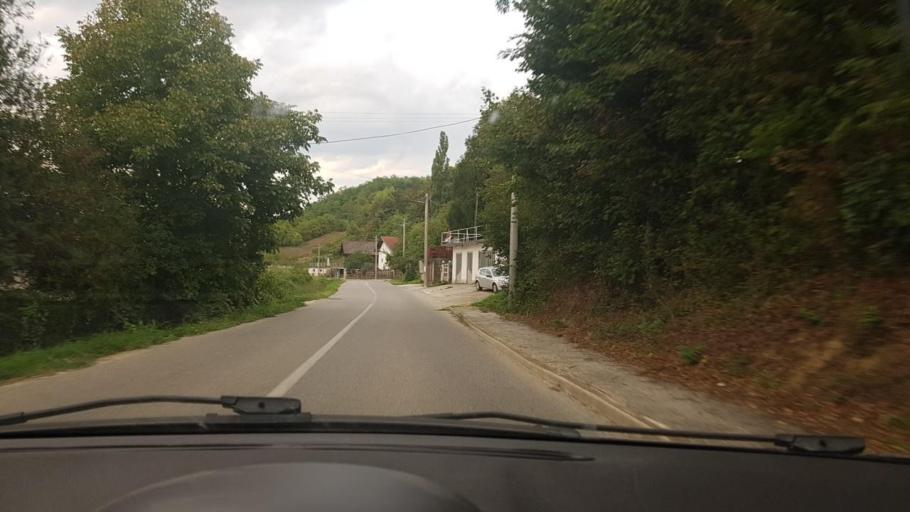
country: HR
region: Grad Zagreb
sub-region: Sesvete
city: Sesvete
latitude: 45.9194
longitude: 16.1704
